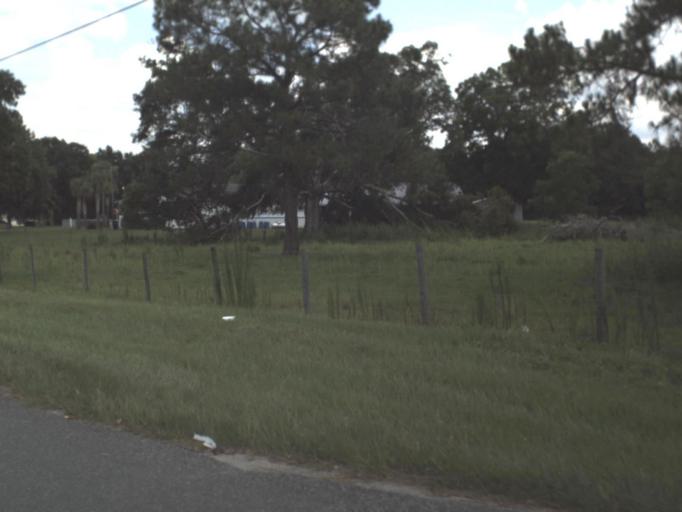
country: US
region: Florida
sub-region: Union County
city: Lake Butler
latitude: 30.0617
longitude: -82.2407
